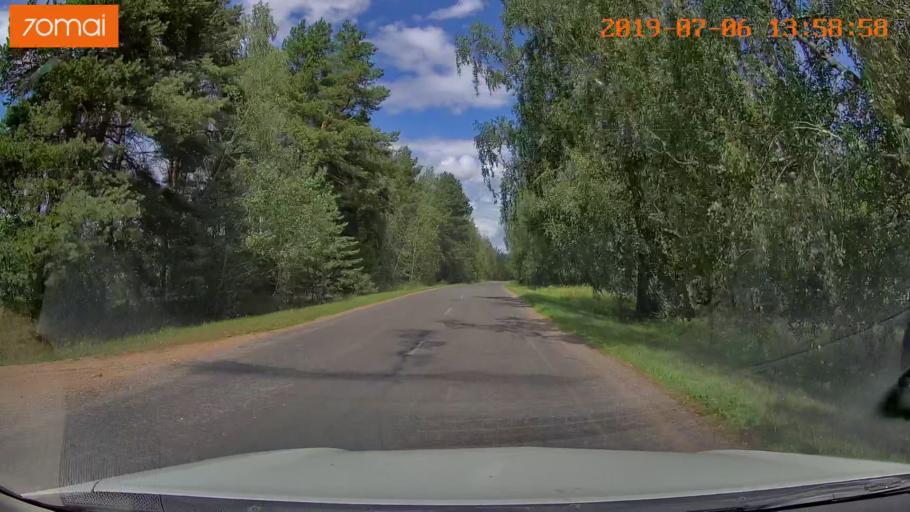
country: BY
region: Minsk
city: Ivyanyets
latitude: 53.7901
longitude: 26.8108
